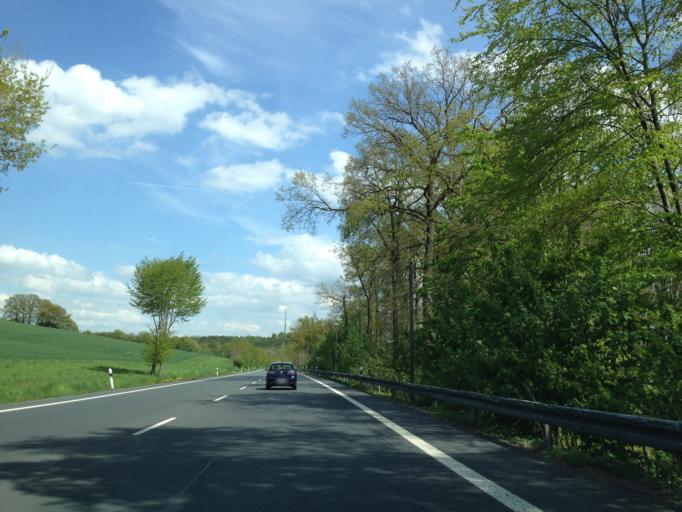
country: DE
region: North Rhine-Westphalia
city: Warstein
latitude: 51.4928
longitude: 8.3092
